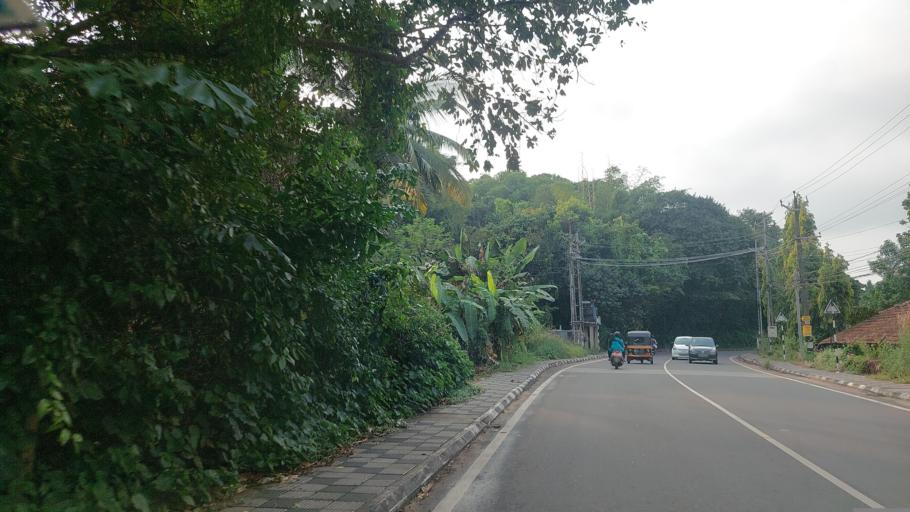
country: IN
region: Kerala
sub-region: Kozhikode
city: Kozhikode
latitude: 11.2912
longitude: 75.7715
